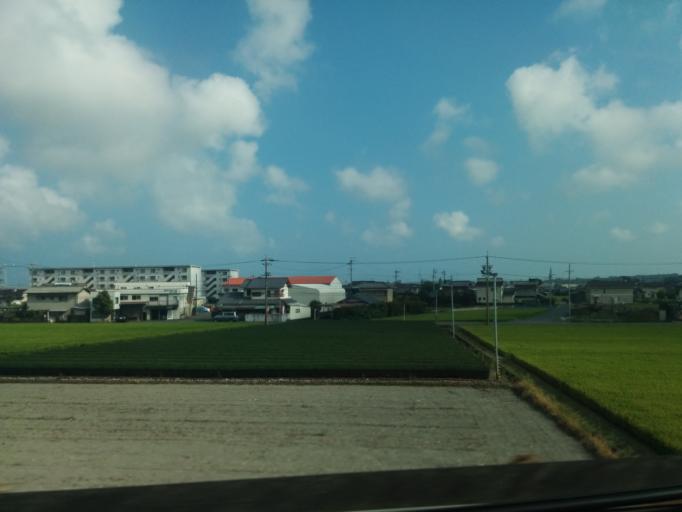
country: JP
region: Shizuoka
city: Shimada
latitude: 34.8131
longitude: 138.2201
